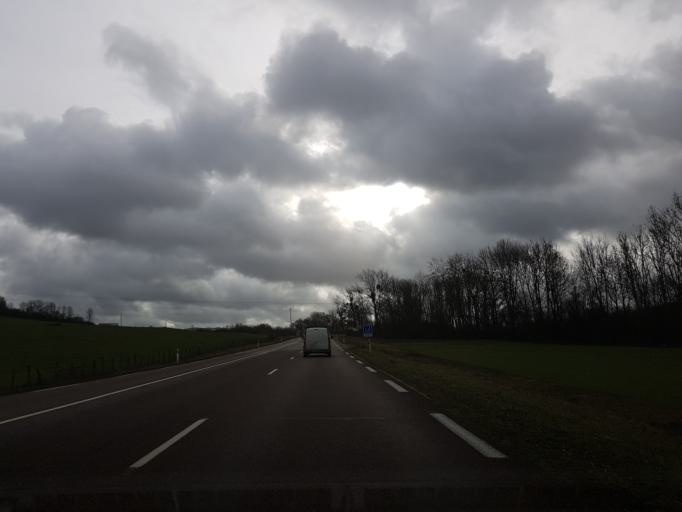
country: FR
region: Champagne-Ardenne
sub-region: Departement de la Haute-Marne
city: Langres
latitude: 47.8795
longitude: 5.3210
